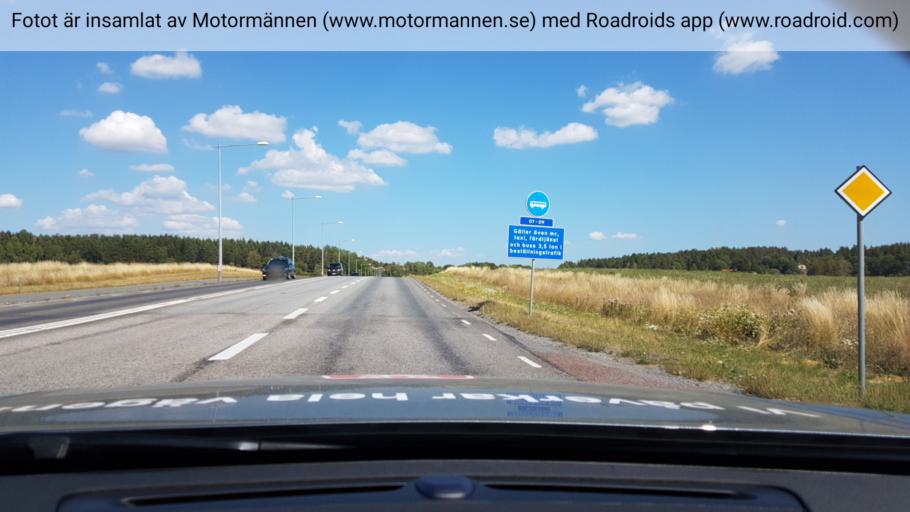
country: SE
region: Stockholm
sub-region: Ekero Kommun
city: Ekeroe
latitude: 59.3028
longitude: 17.8553
